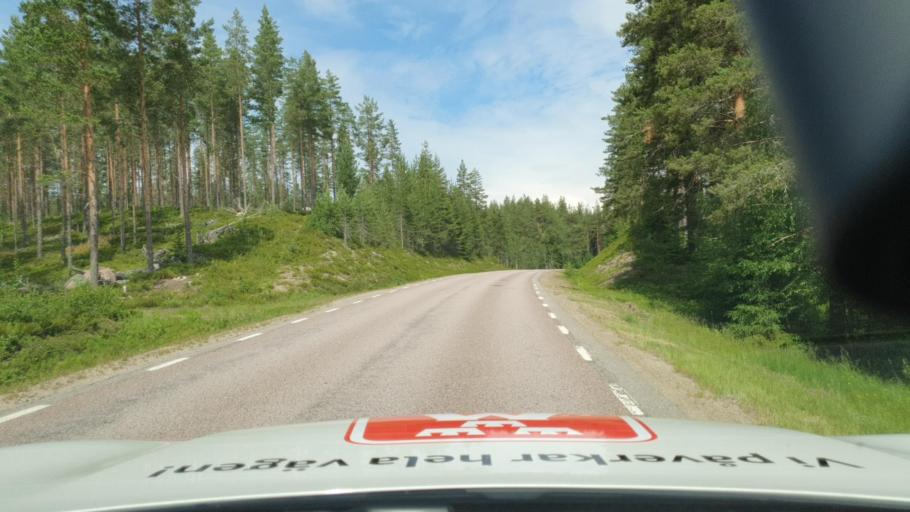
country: NO
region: Hedmark
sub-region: Asnes
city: Flisa
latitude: 60.7324
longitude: 12.6211
